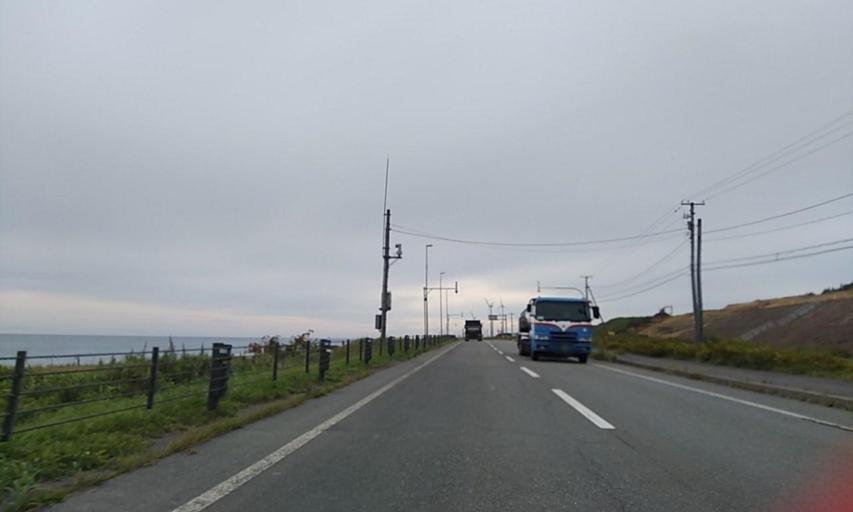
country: JP
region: Hokkaido
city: Makubetsu
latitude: 45.3702
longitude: 142.1072
